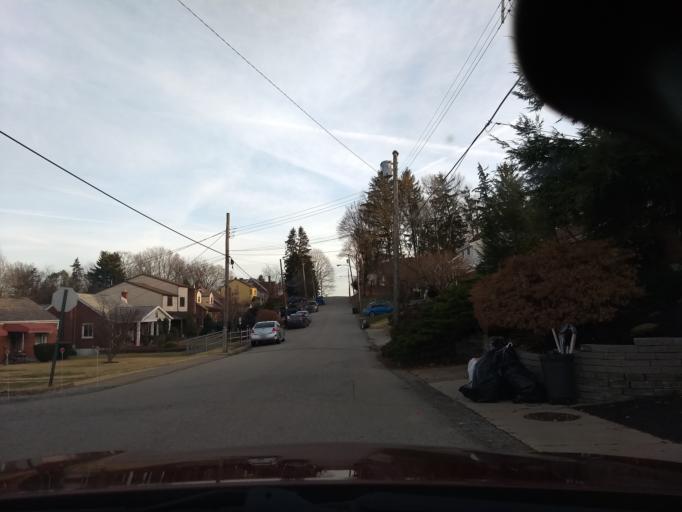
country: US
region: Pennsylvania
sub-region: Allegheny County
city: Dravosburg
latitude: 40.3539
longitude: -79.9090
